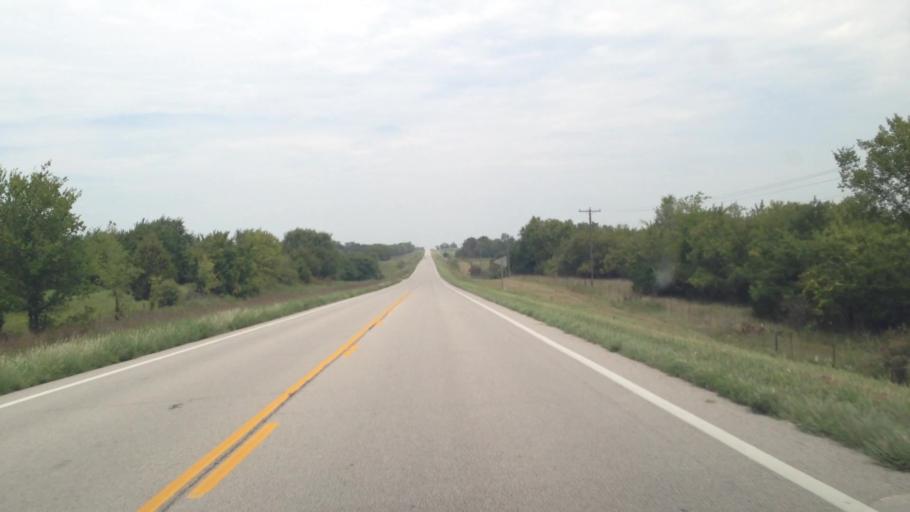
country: US
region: Kansas
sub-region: Neosho County
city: Erie
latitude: 37.6577
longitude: -95.2517
